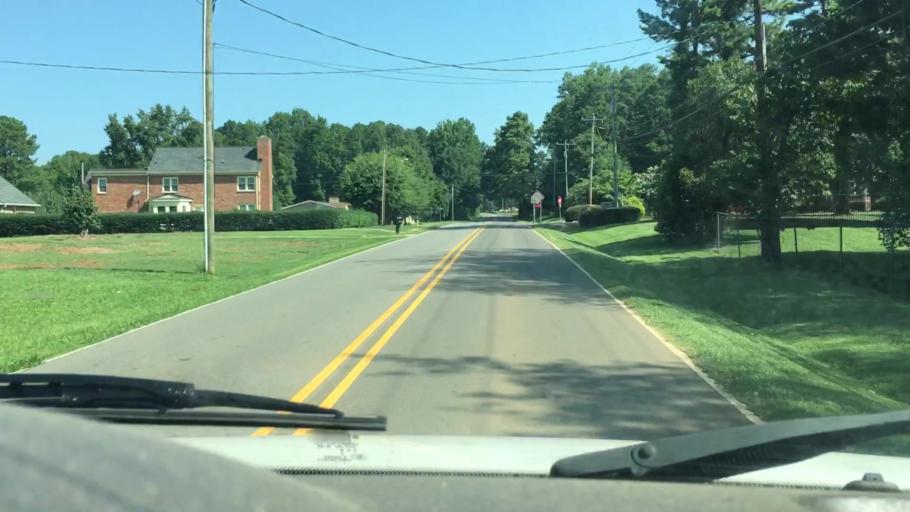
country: US
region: North Carolina
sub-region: Mecklenburg County
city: Huntersville
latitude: 35.3251
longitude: -80.8518
